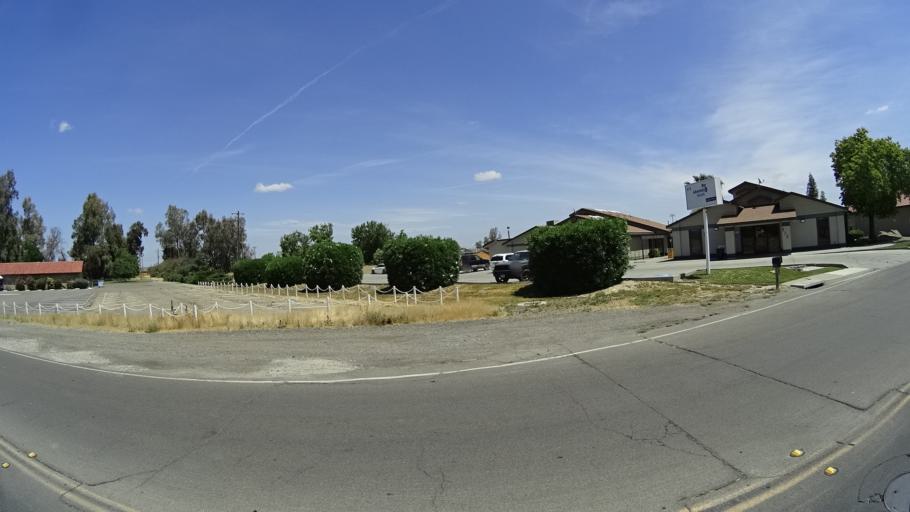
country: US
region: California
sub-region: Kings County
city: Lemoore
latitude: 36.3007
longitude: -119.7697
